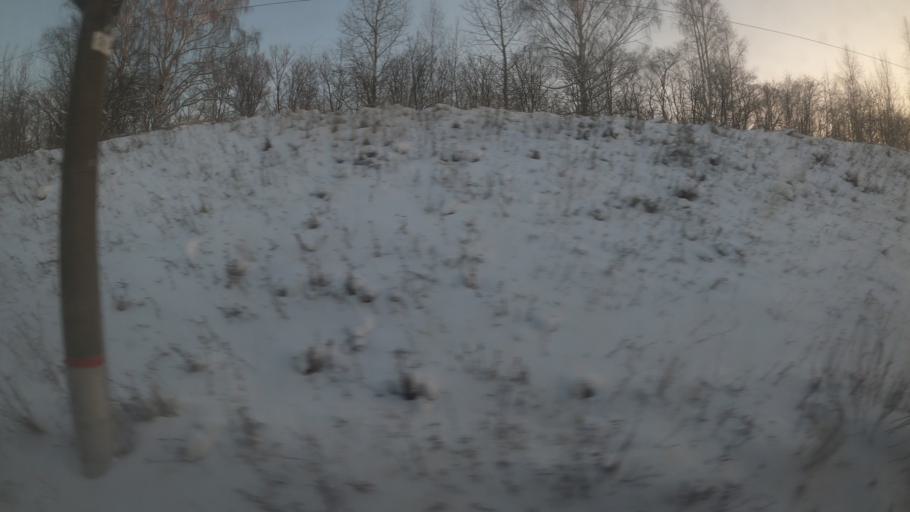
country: RU
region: Moskovskaya
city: Dedenevo
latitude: 56.2661
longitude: 37.5106
